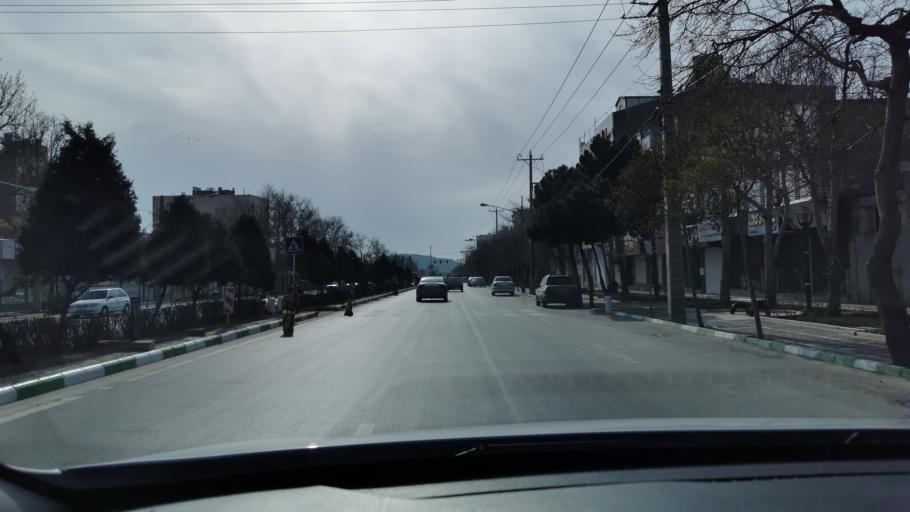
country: IR
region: Razavi Khorasan
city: Mashhad
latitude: 36.2884
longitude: 59.5421
